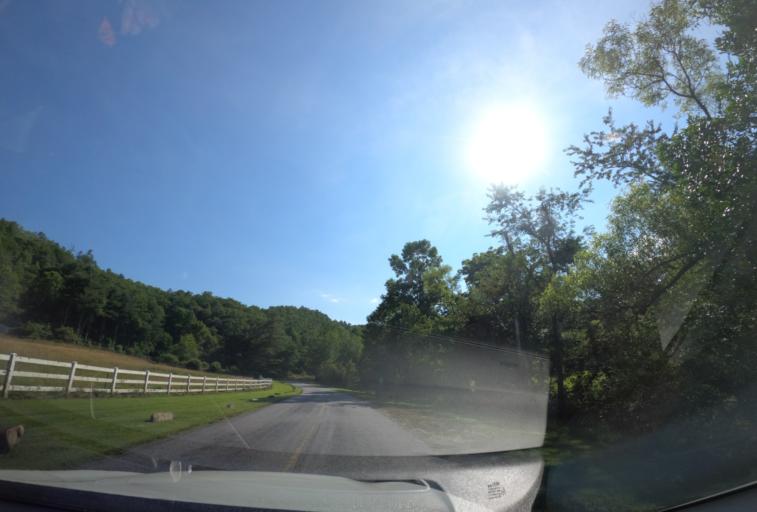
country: US
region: North Carolina
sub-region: Transylvania County
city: Brevard
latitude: 35.2260
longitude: -82.6441
